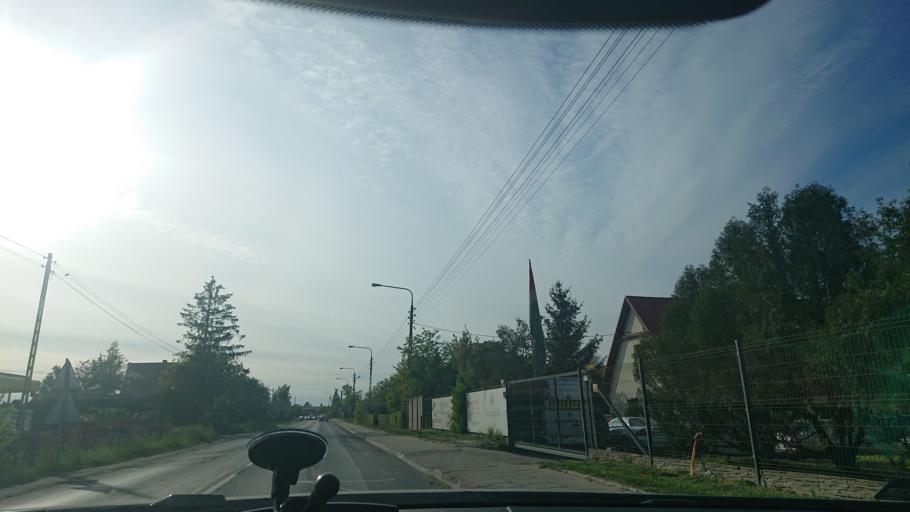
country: PL
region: Greater Poland Voivodeship
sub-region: Powiat gnieznienski
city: Gniezno
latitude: 52.5421
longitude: 17.5770
